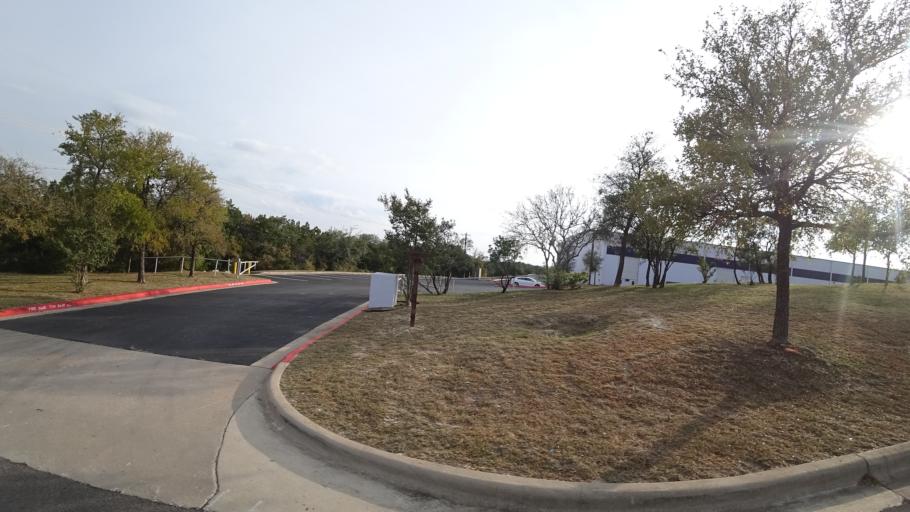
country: US
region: Texas
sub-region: Travis County
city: Hudson Bend
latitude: 30.3825
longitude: -97.8730
